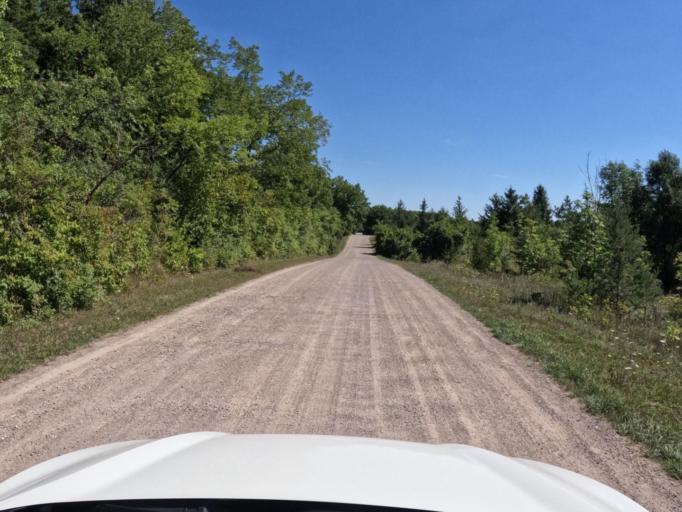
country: CA
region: Ontario
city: Cambridge
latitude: 43.4233
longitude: -80.2540
